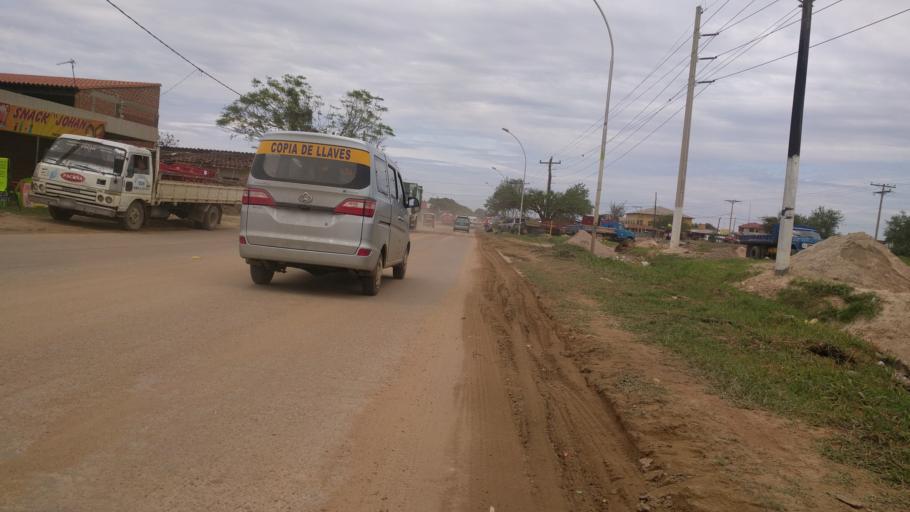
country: BO
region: Santa Cruz
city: Santa Cruz de la Sierra
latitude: -17.8511
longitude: -63.1801
